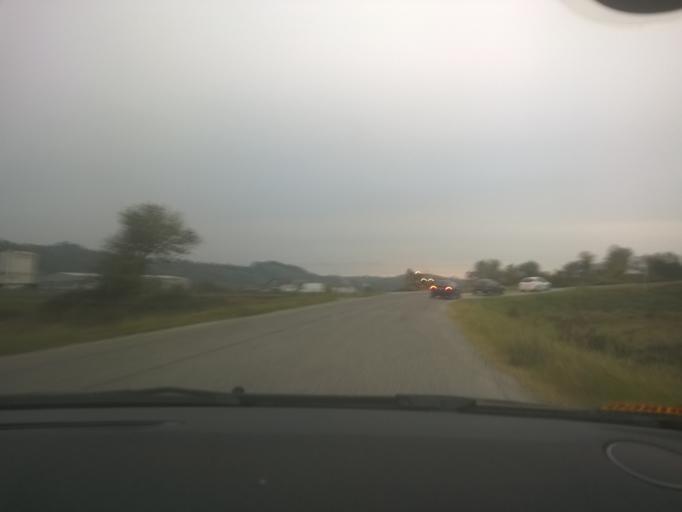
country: HR
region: Zagrebacka
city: Pojatno
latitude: 45.9105
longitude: 15.8155
